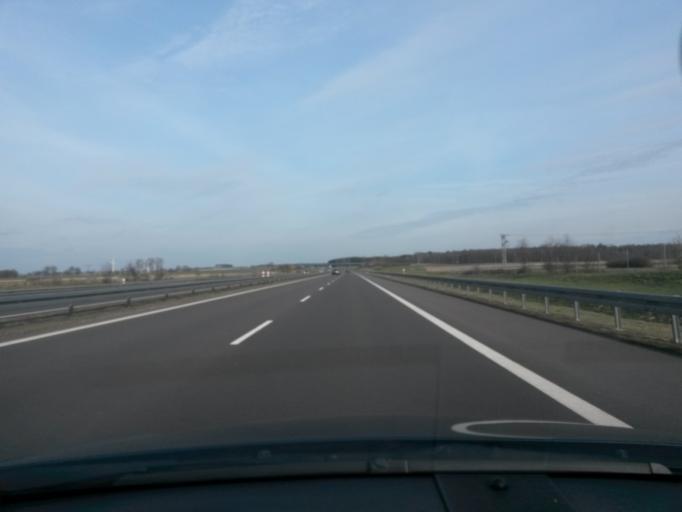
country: PL
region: Greater Poland Voivodeship
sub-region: Powiat sredzki
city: Dominowo
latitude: 52.3098
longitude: 17.3476
